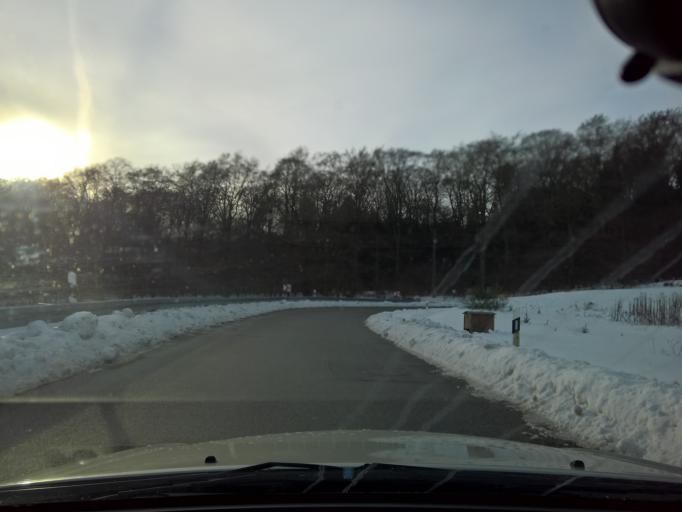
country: DE
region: Hesse
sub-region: Regierungsbezirk Darmstadt
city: Schlangenbad
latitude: 50.0960
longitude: 8.0671
